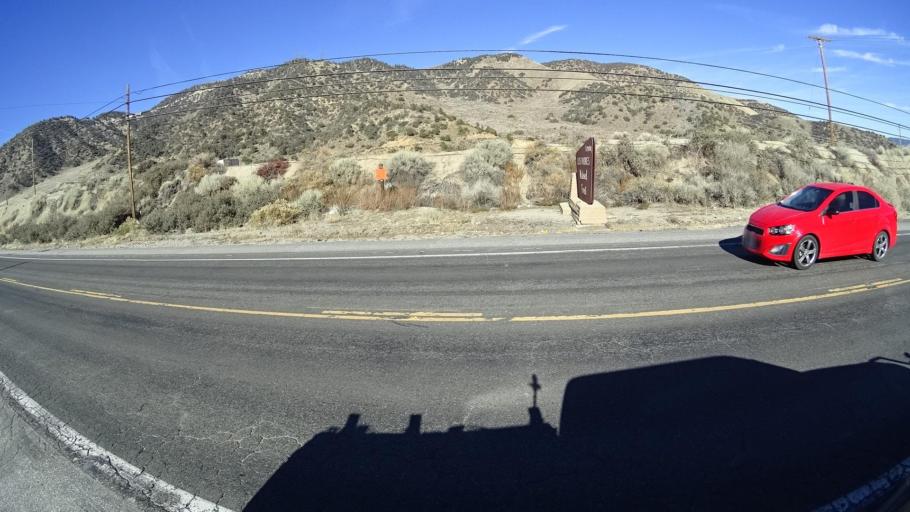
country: US
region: California
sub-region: Kern County
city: Frazier Park
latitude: 34.8182
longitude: -118.9142
